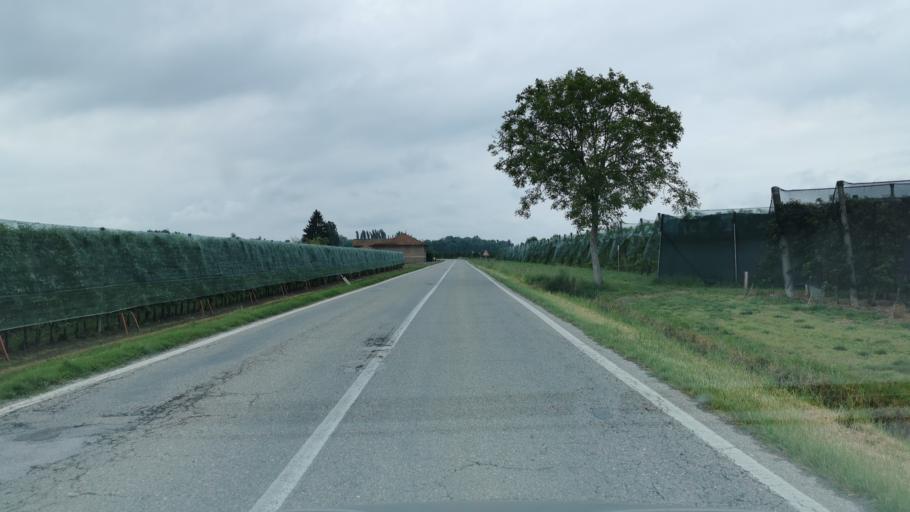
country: IT
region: Piedmont
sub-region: Provincia di Cuneo
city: Genola
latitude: 44.6165
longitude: 7.6284
